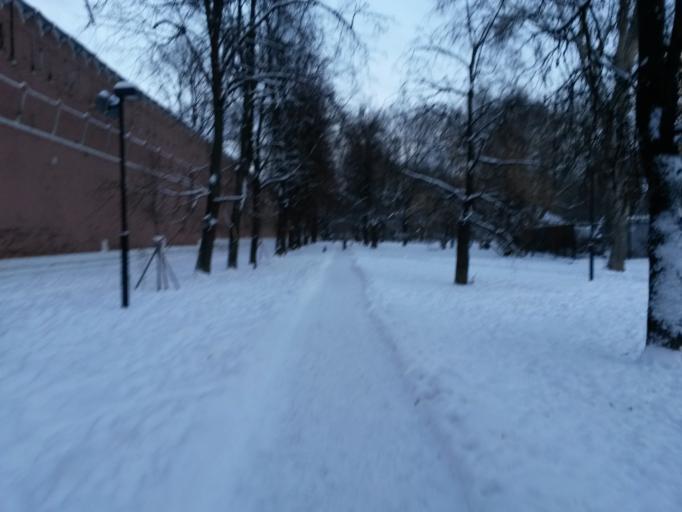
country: RU
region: Moscow
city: Novyye Cheremushki
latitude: 55.7144
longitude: 37.6045
